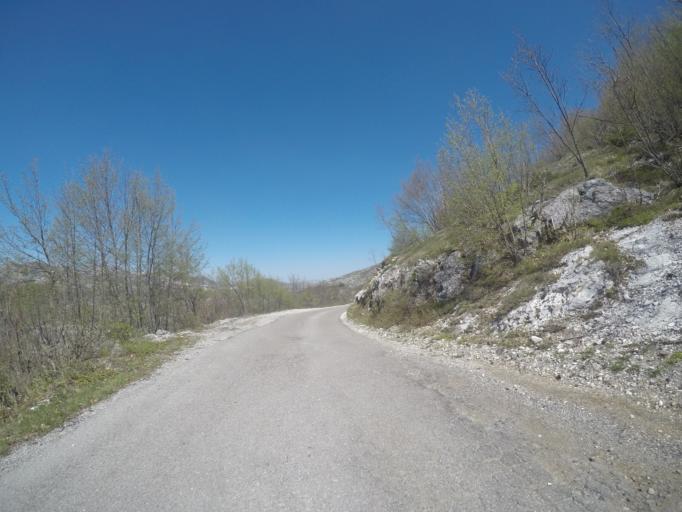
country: ME
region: Cetinje
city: Cetinje
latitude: 42.4488
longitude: 18.8735
